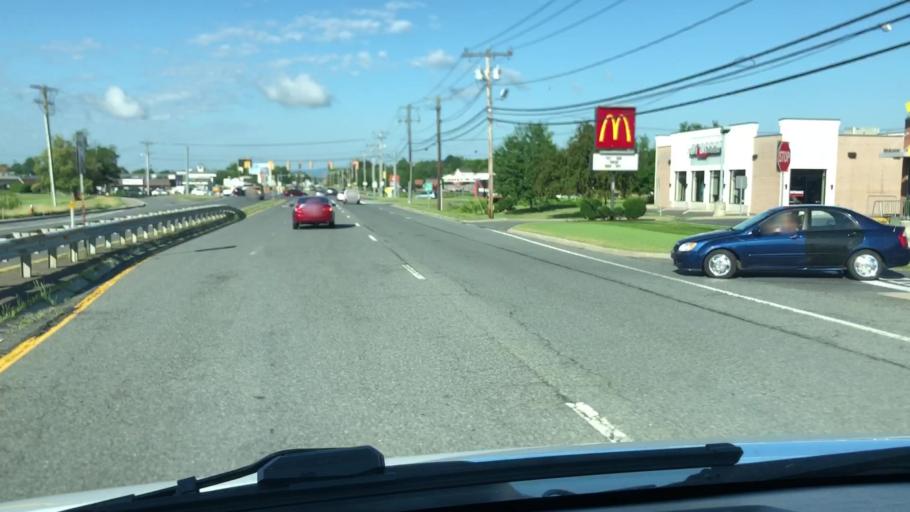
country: US
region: Massachusetts
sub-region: Hampshire County
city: Amherst Center
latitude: 42.3587
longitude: -72.5492
